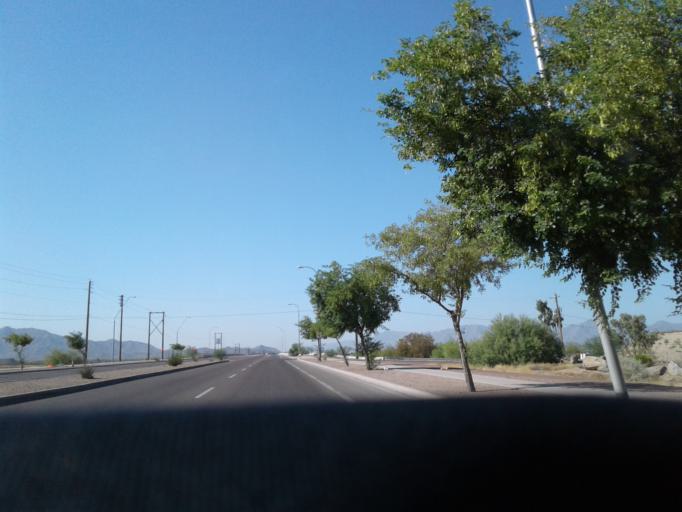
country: US
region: Arizona
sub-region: Maricopa County
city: Laveen
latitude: 33.4105
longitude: -112.1692
